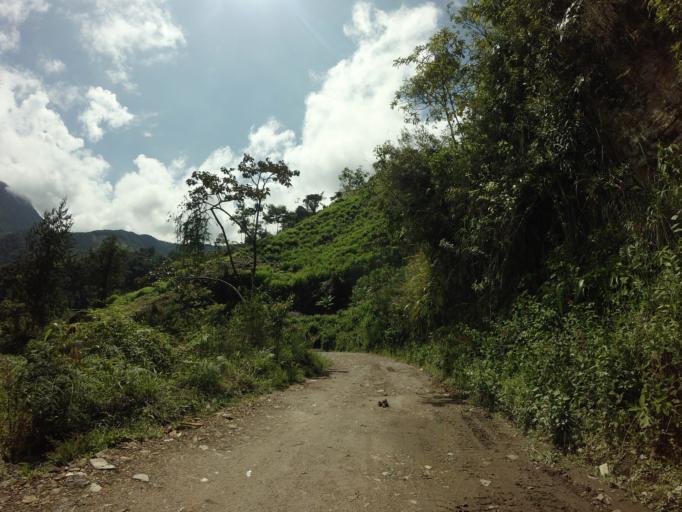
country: CO
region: Caldas
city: Pensilvania
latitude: 5.4637
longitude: -75.1817
